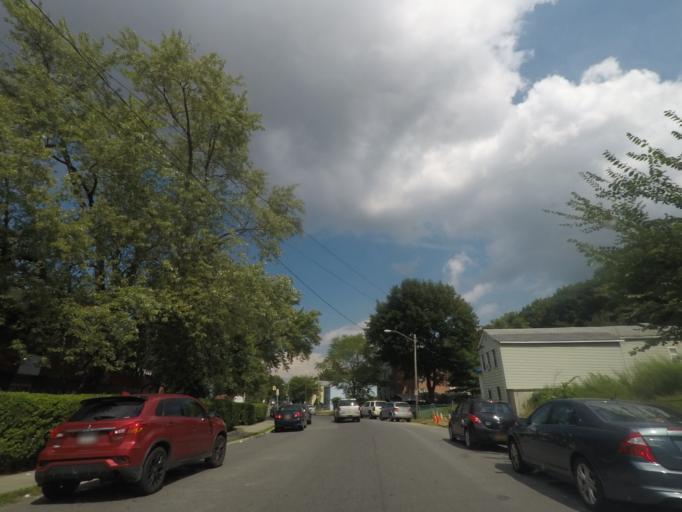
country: US
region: New York
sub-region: Rensselaer County
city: Troy
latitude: 42.7162
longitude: -73.6925
